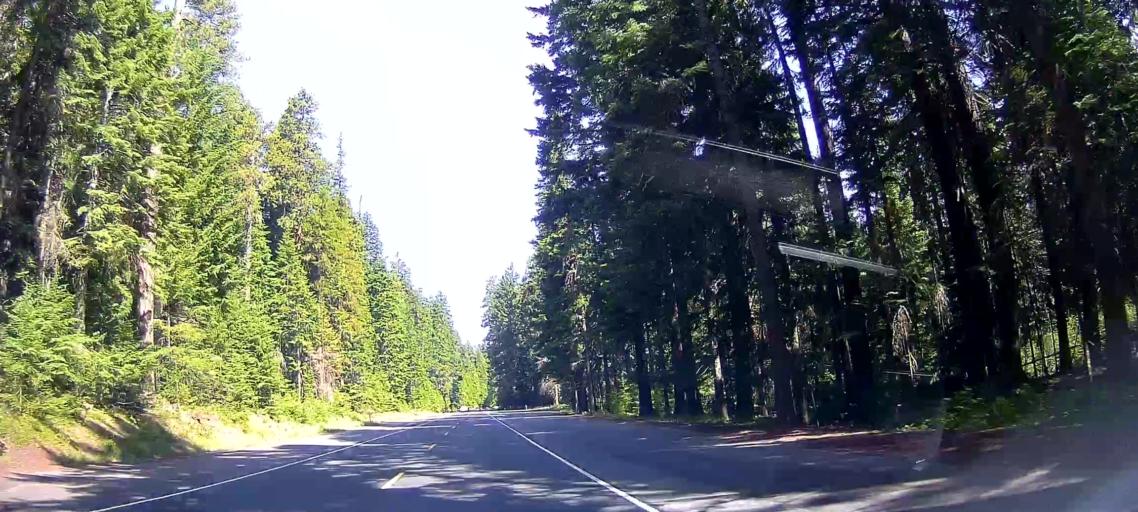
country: US
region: Oregon
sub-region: Jefferson County
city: Warm Springs
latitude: 45.0917
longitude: -121.5496
